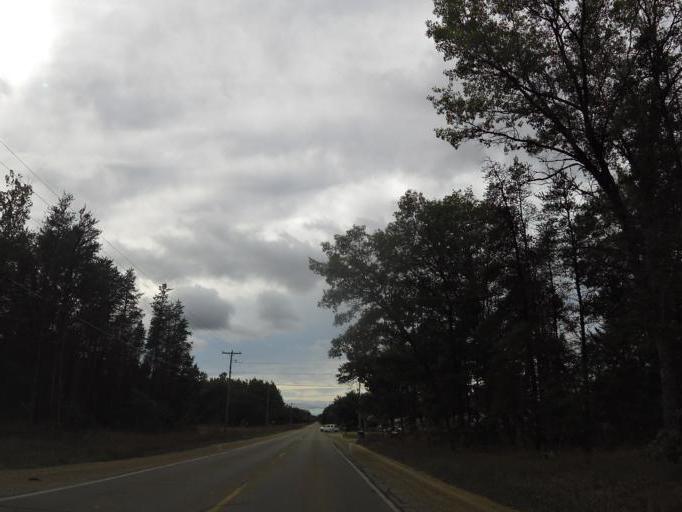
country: US
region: Michigan
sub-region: Roscommon County
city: Saint Helen
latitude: 44.3490
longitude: -84.4299
